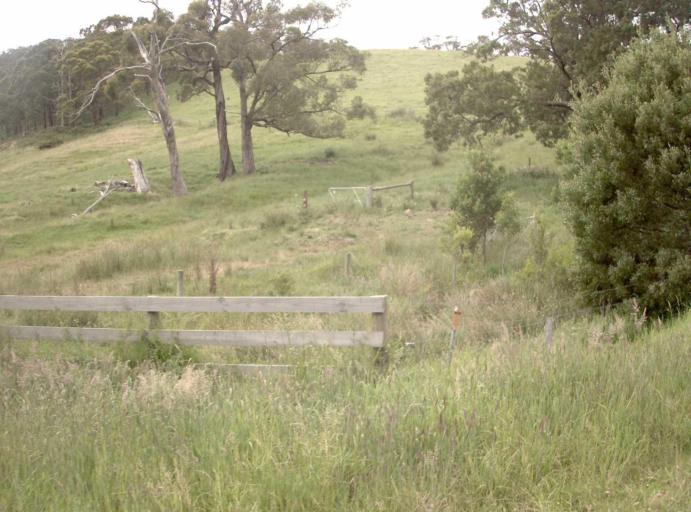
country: AU
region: Victoria
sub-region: Bass Coast
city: North Wonthaggi
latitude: -38.5223
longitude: 145.7008
